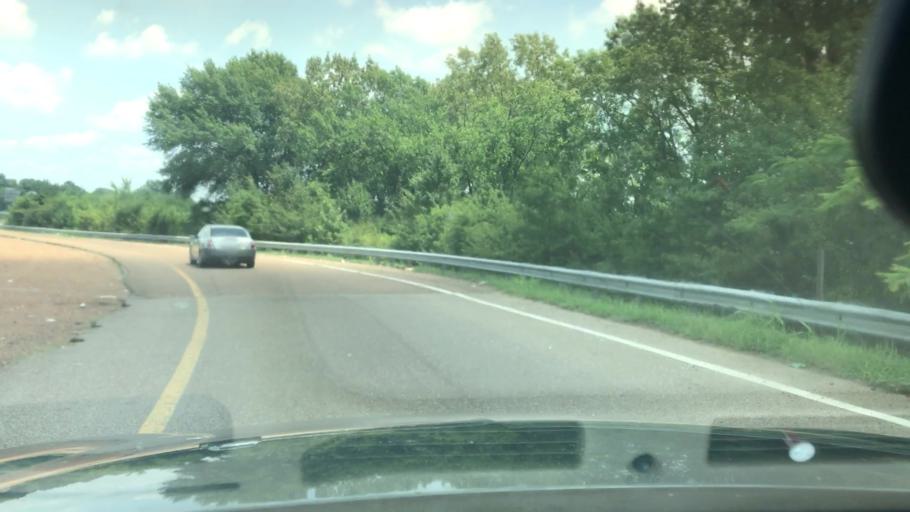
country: US
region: Tennessee
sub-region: Shelby County
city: Germantown
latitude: 35.0784
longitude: -89.9304
